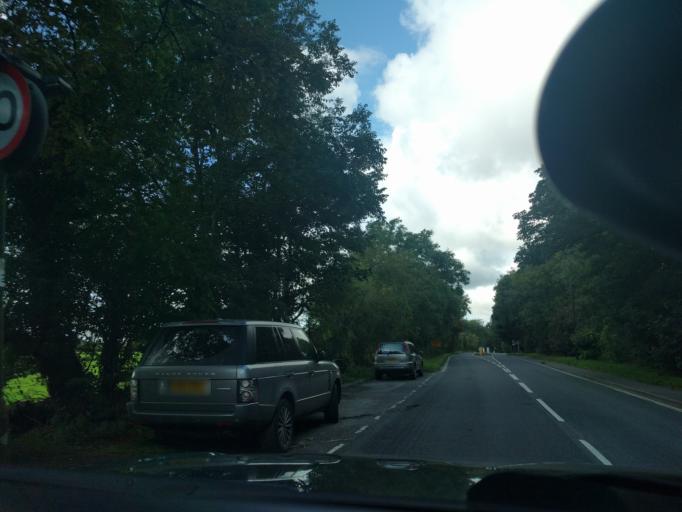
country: GB
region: England
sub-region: Bath and North East Somerset
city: Bath
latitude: 51.3732
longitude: -2.3248
